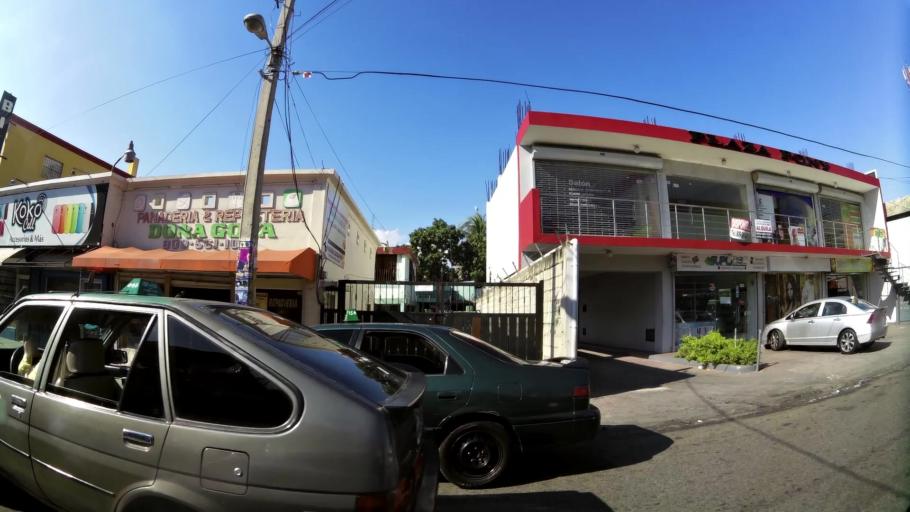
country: DO
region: Nacional
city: Santo Domingo
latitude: 18.4763
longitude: -69.9726
